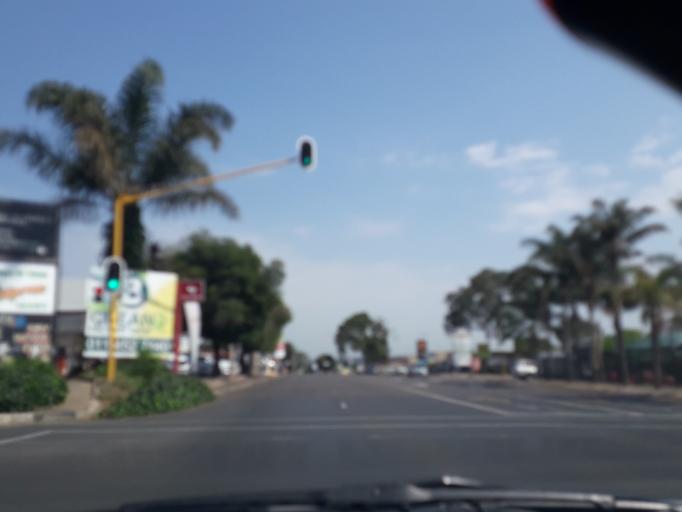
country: ZA
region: Gauteng
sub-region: City of Johannesburg Metropolitan Municipality
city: Modderfontein
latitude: -26.1317
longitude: 28.1784
